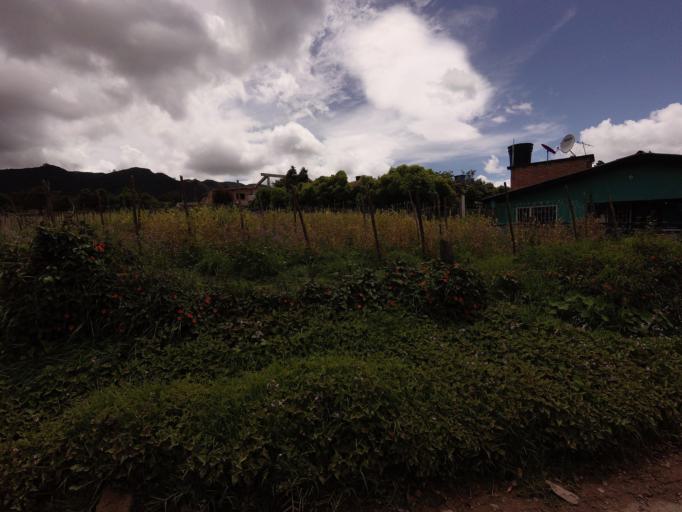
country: CO
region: Cundinamarca
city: Tabio
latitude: 4.9746
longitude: -74.0702
